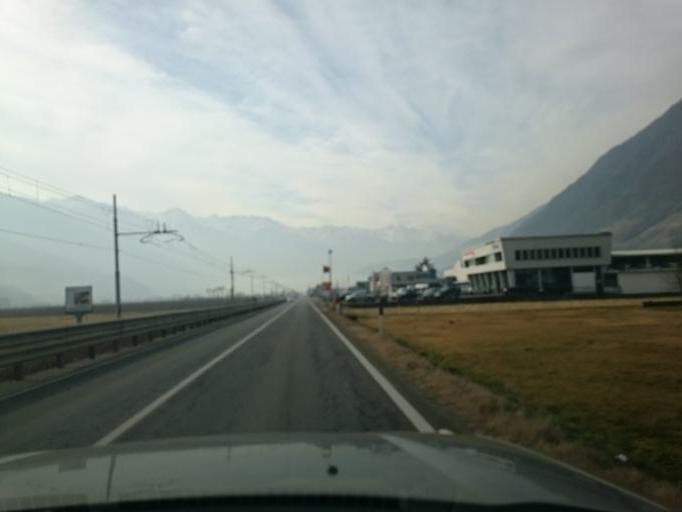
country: IT
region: Lombardy
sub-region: Provincia di Sondrio
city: Villa
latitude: 46.2059
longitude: 10.1413
